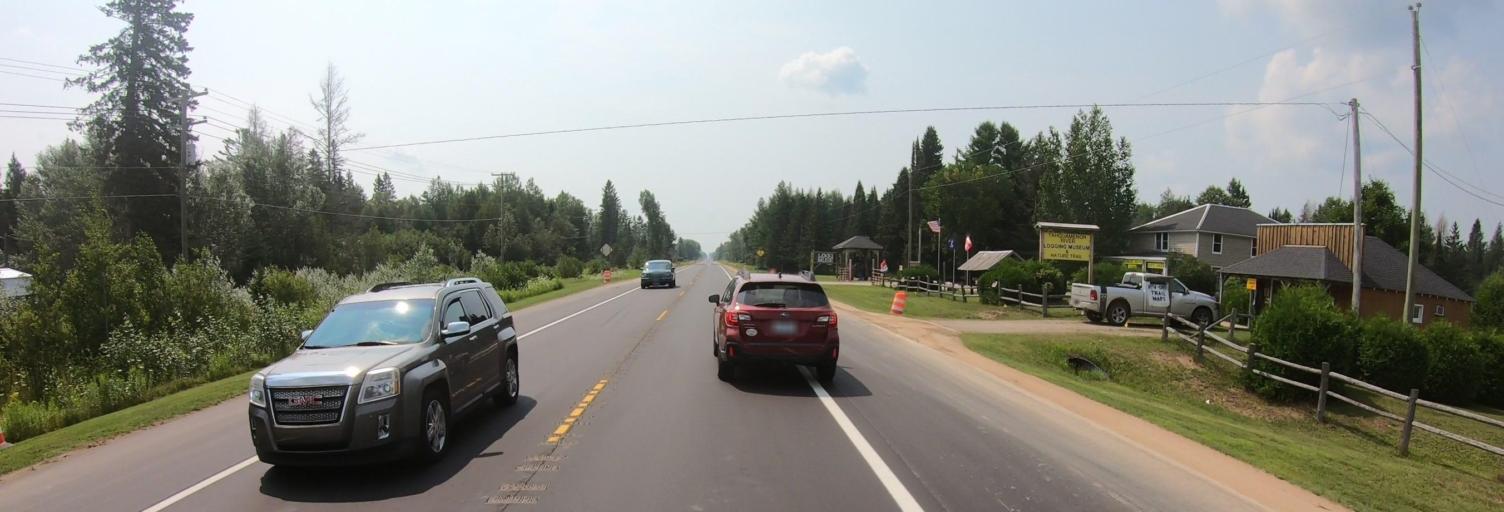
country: US
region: Michigan
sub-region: Luce County
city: Newberry
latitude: 46.3709
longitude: -85.5099
